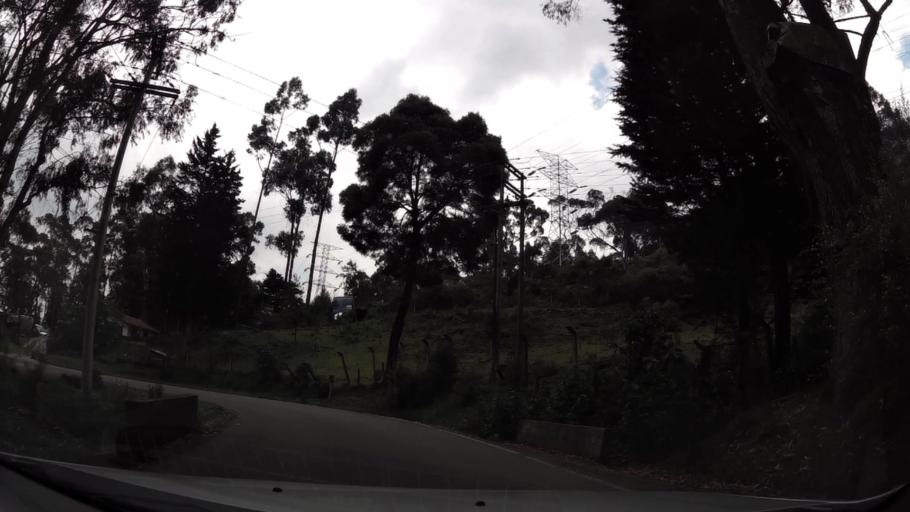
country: CO
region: Bogota D.C.
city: Bogota
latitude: 4.5882
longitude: -74.0627
